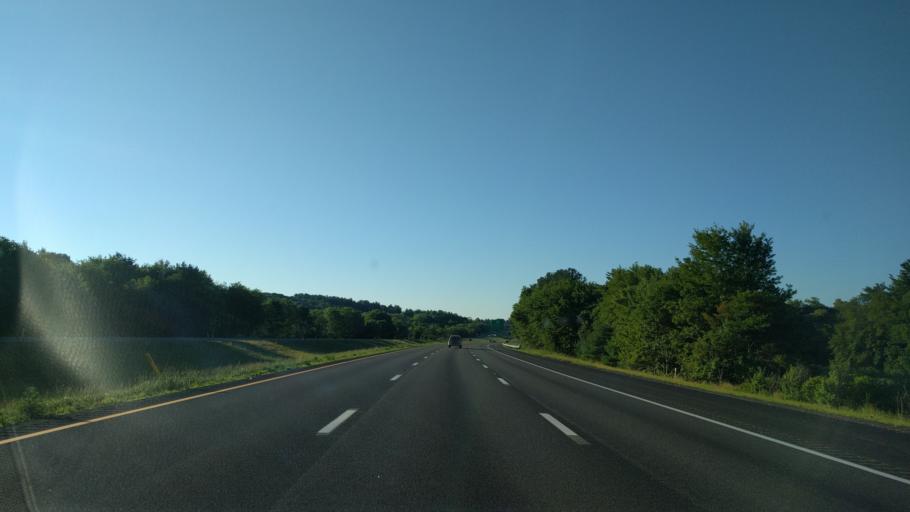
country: US
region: Massachusetts
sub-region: Norfolk County
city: Bellingham
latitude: 42.0990
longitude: -71.4378
